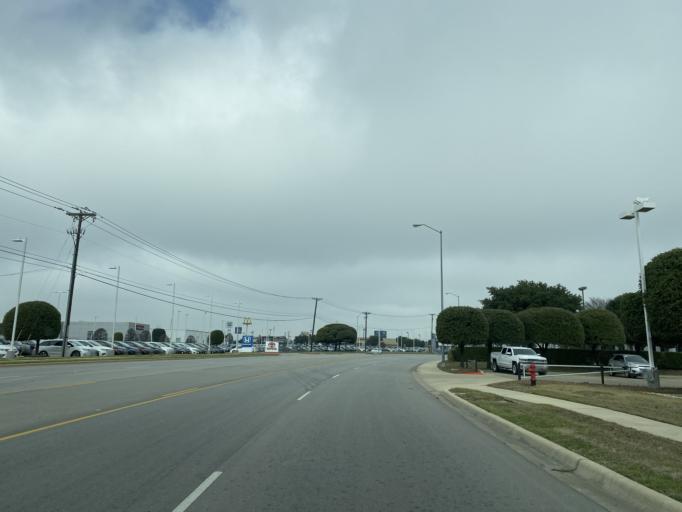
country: US
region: Texas
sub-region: Williamson County
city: Round Rock
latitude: 30.5322
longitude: -97.6896
